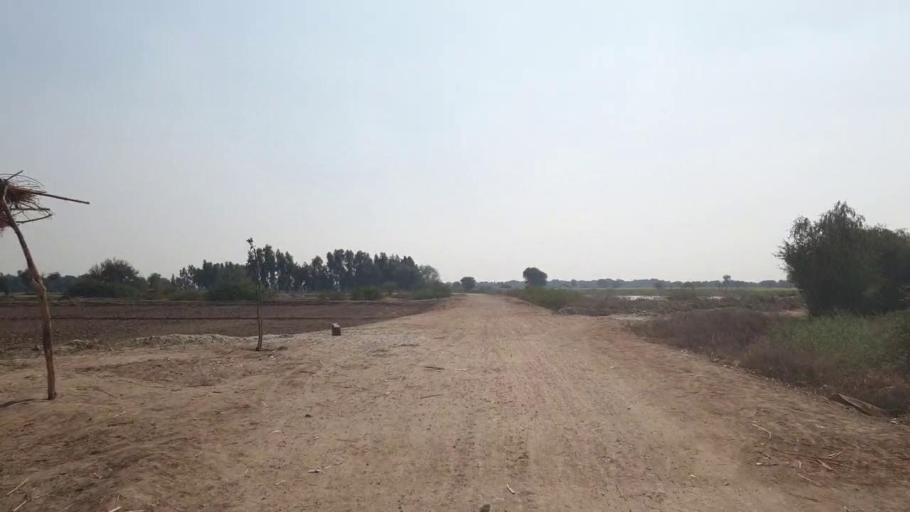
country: PK
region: Sindh
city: Chambar
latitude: 25.3538
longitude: 68.8987
